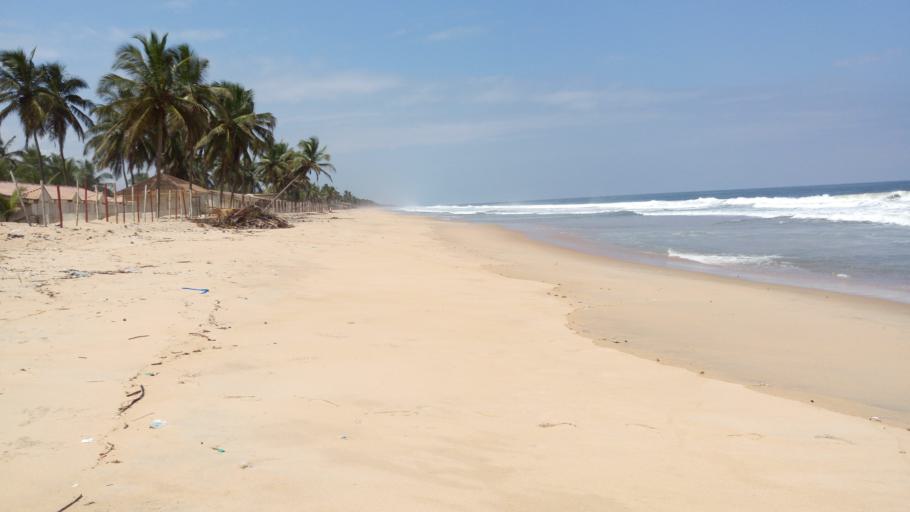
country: CI
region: Sud-Comoe
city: Grand-Bassam
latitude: 5.1872
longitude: -3.6926
